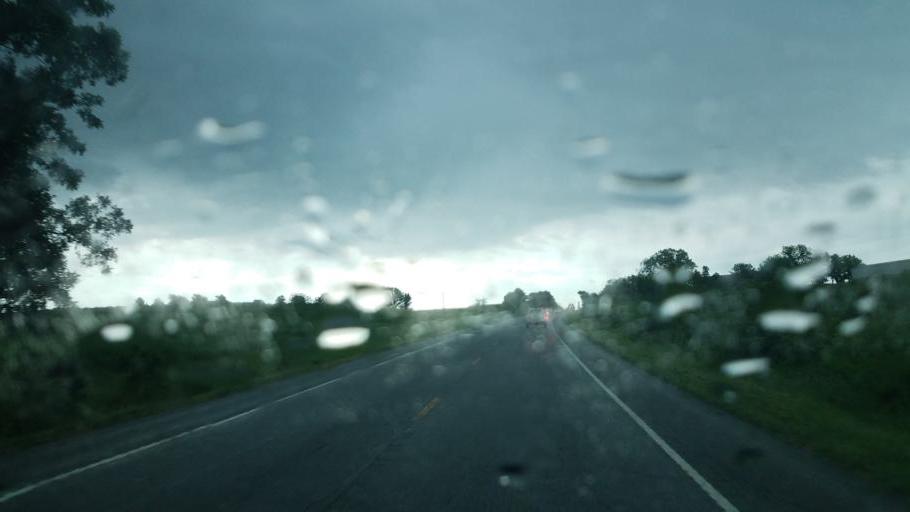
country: US
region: Missouri
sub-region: Cooper County
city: Boonville
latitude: 38.8987
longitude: -92.6664
